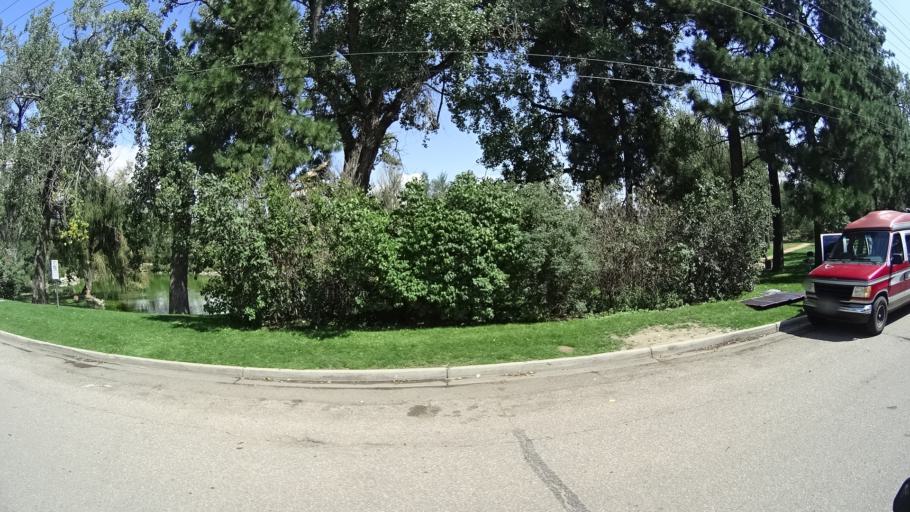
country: US
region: Colorado
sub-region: El Paso County
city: Colorado Springs
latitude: 38.8486
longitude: -104.8304
